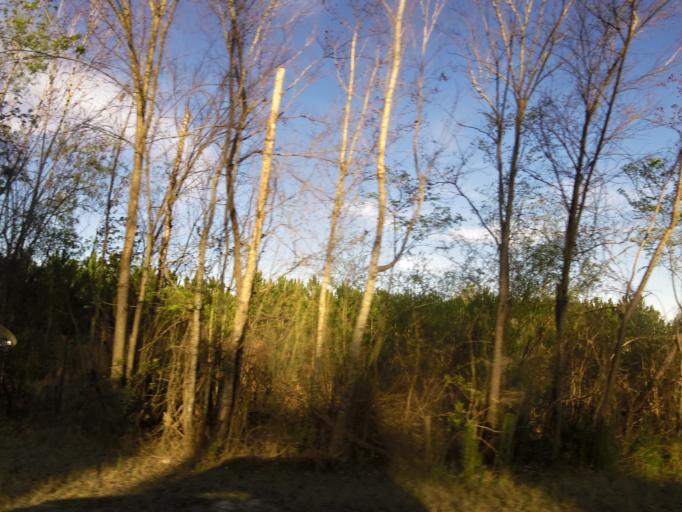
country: US
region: Florida
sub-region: Duval County
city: Jacksonville
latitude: 30.4295
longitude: -81.6026
